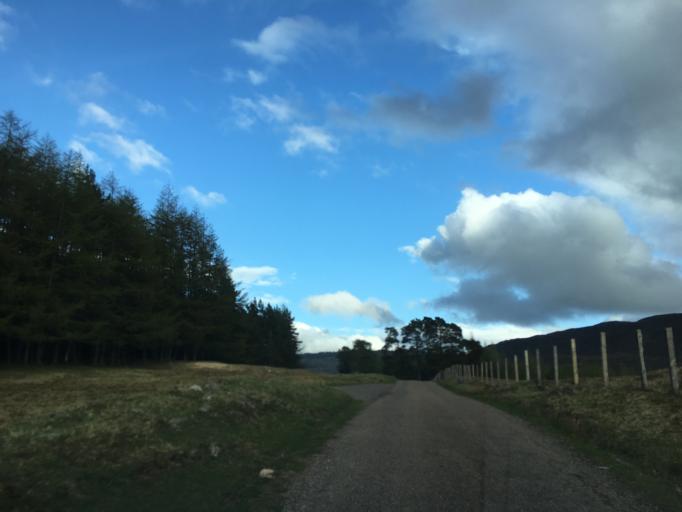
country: GB
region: Scotland
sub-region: Highland
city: Kingussie
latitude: 57.0092
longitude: -4.4076
